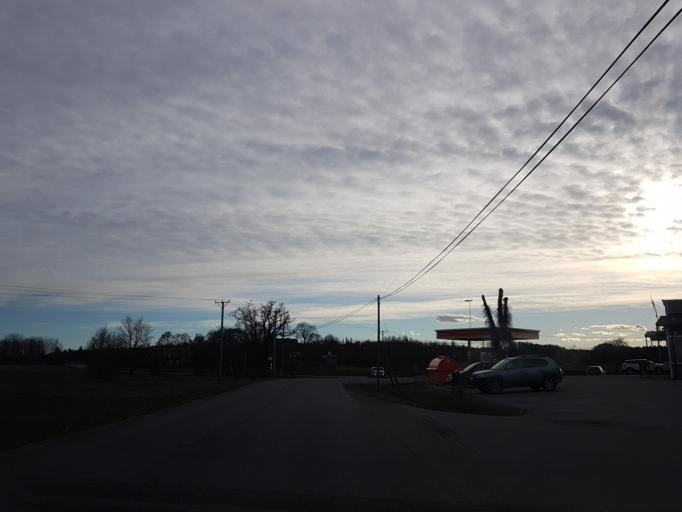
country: SE
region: Stockholm
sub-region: Vallentuna Kommun
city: Vallentuna
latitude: 59.6696
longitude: 18.0498
